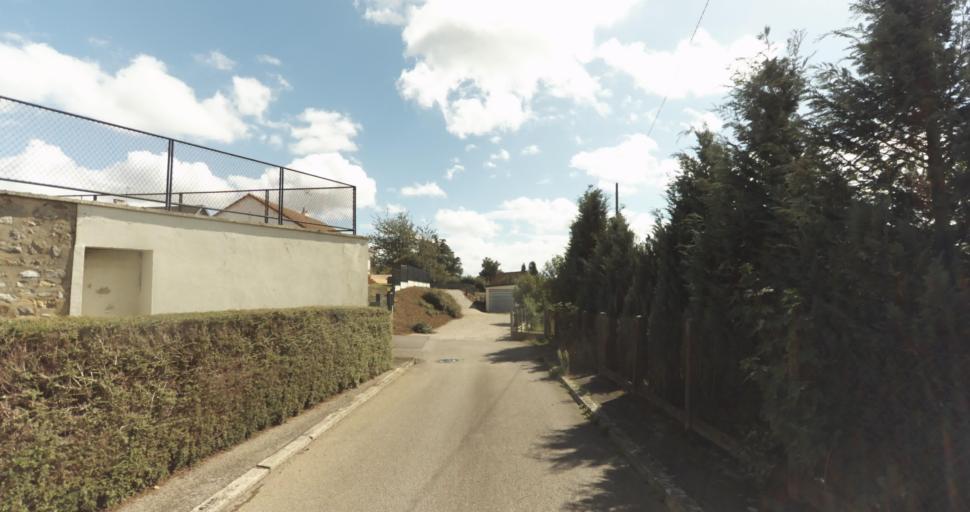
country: FR
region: Lower Normandy
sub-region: Departement de l'Orne
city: Gace
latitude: 48.7871
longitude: 0.2949
